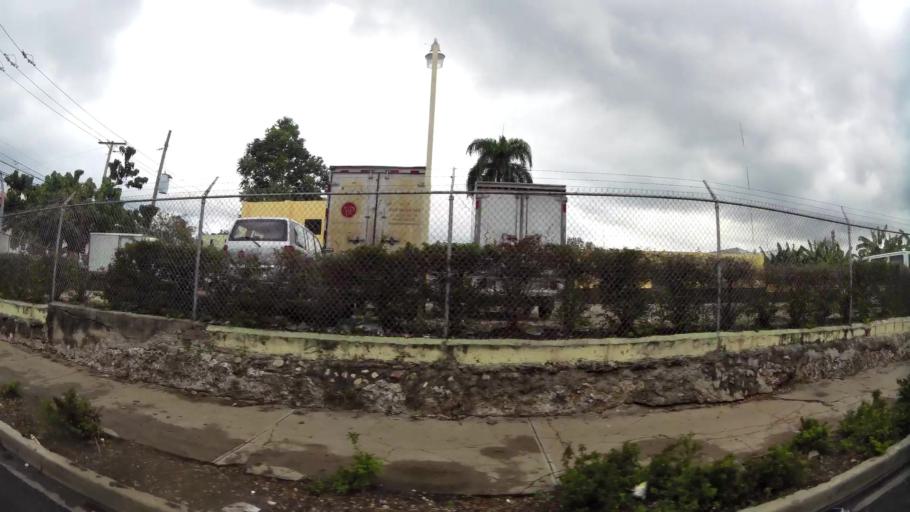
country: DO
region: Nacional
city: La Agustina
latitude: 18.4870
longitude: -69.9325
